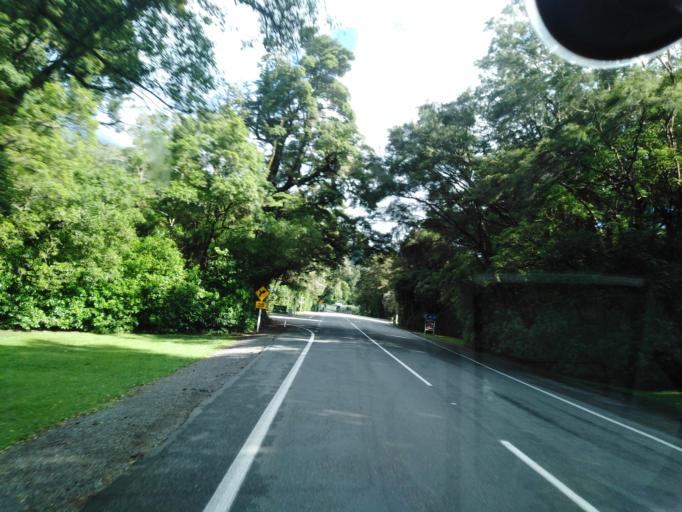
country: NZ
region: Nelson
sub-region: Nelson City
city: Nelson
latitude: -41.2998
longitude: 173.5729
